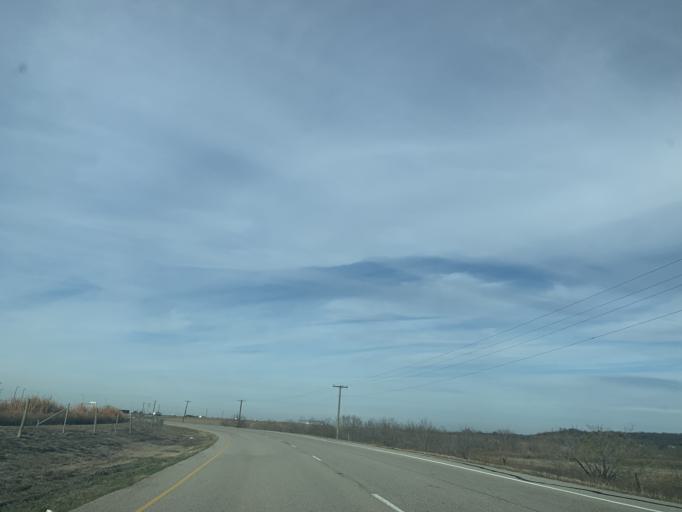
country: US
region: Texas
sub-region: Bell County
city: Salado
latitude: 30.9030
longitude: -97.5568
